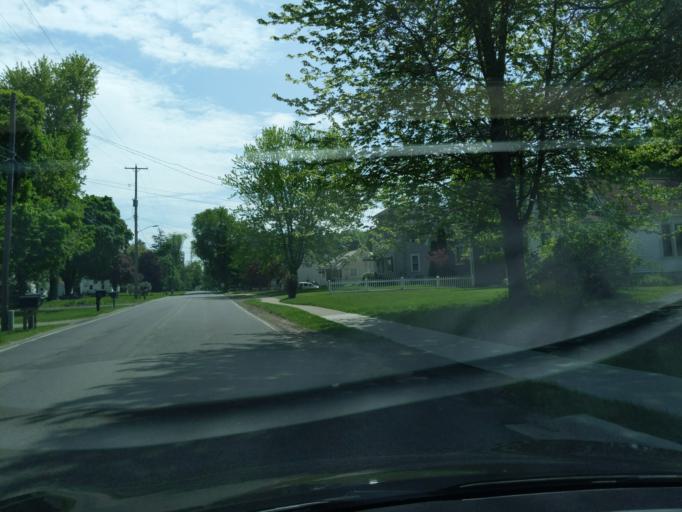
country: US
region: Michigan
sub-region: Ingham County
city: Holt
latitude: 42.6474
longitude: -84.5217
